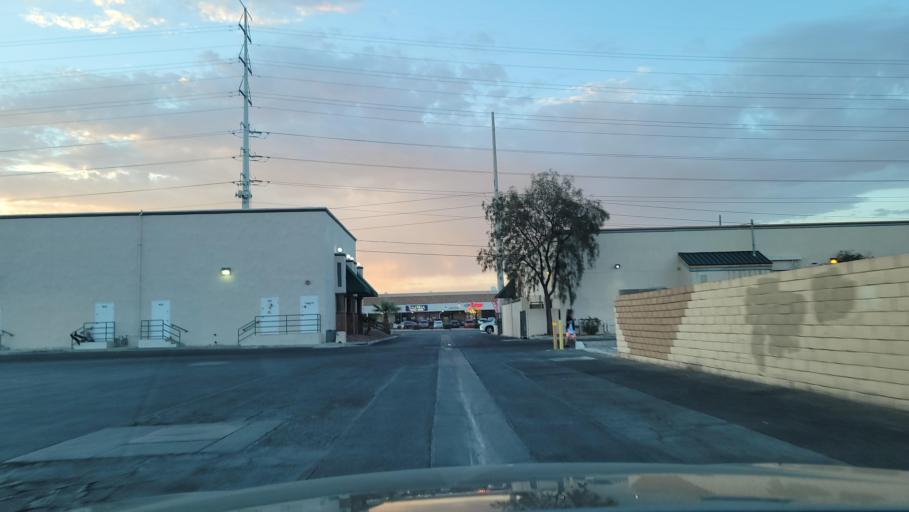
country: US
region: Nevada
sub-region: Clark County
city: Spring Valley
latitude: 36.1136
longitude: -115.2411
